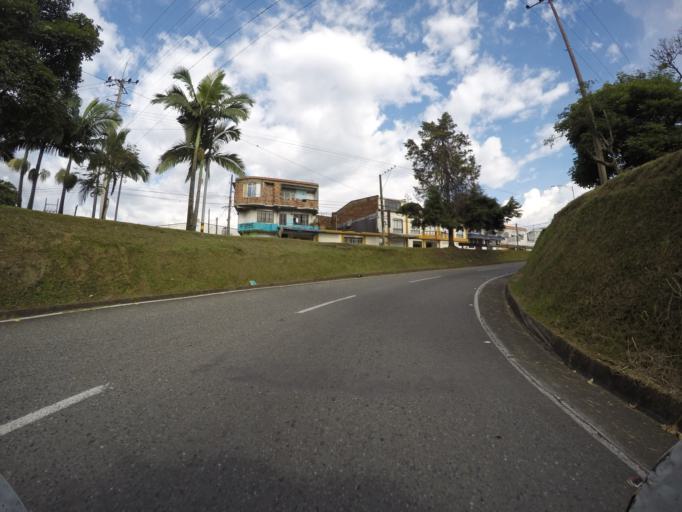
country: CO
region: Risaralda
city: Pereira
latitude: 4.8211
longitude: -75.6845
